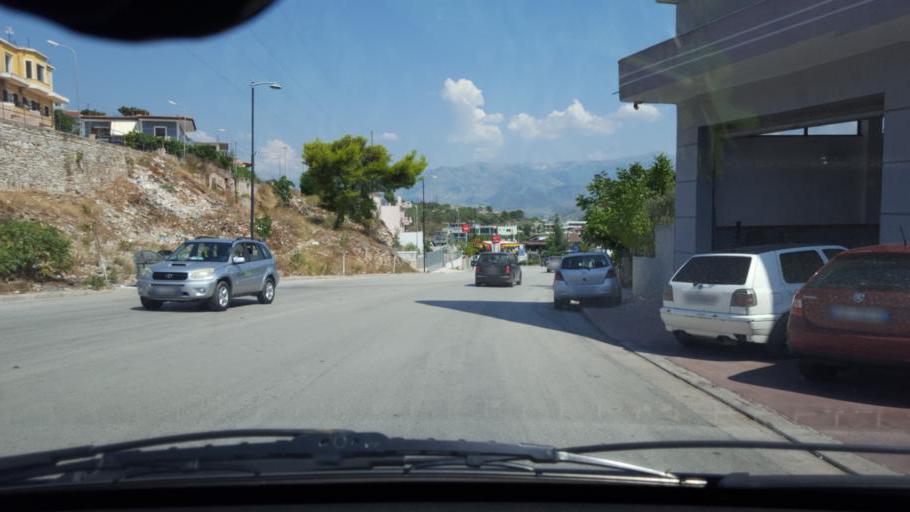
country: AL
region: Vlore
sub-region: Rrethi i Sarandes
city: Sarande
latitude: 39.8706
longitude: 20.0277
